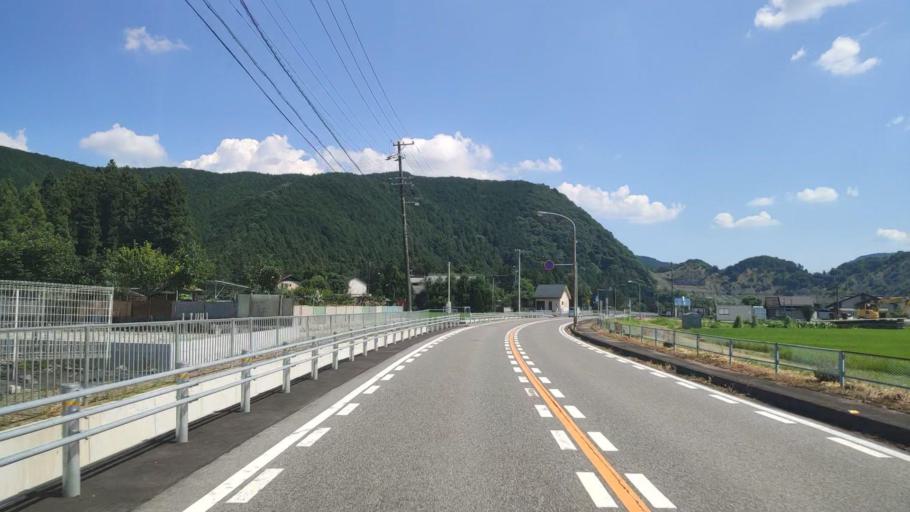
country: JP
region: Gifu
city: Godo
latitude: 35.5355
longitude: 136.6508
